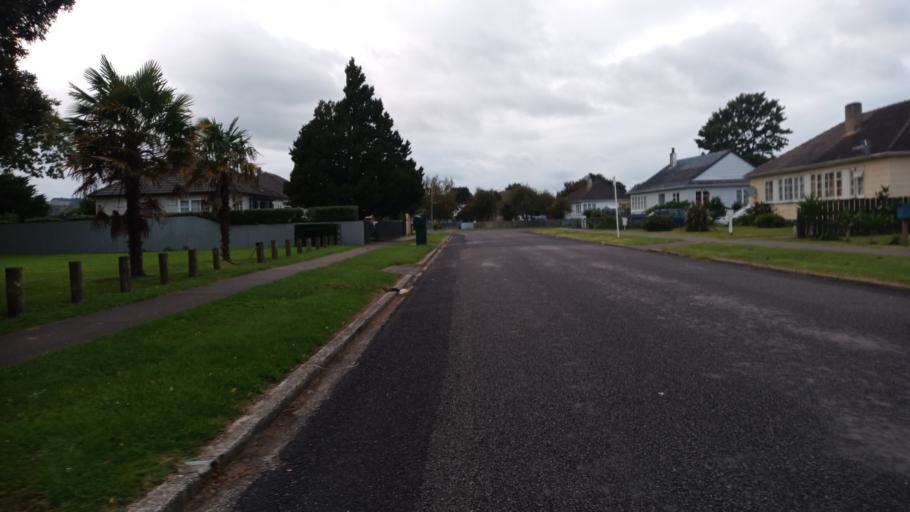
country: NZ
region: Gisborne
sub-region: Gisborne District
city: Gisborne
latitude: -38.6559
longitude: 178.0050
